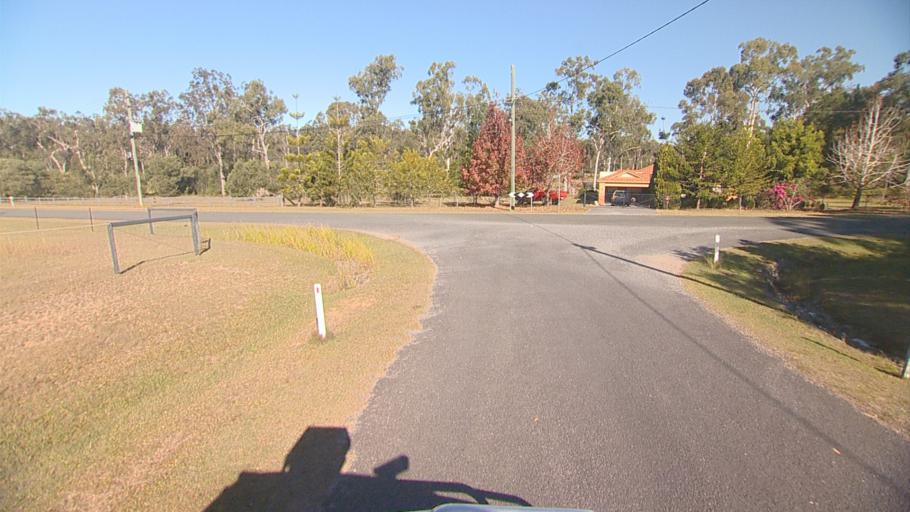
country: AU
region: Queensland
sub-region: Logan
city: Chambers Flat
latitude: -27.7299
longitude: 153.0669
